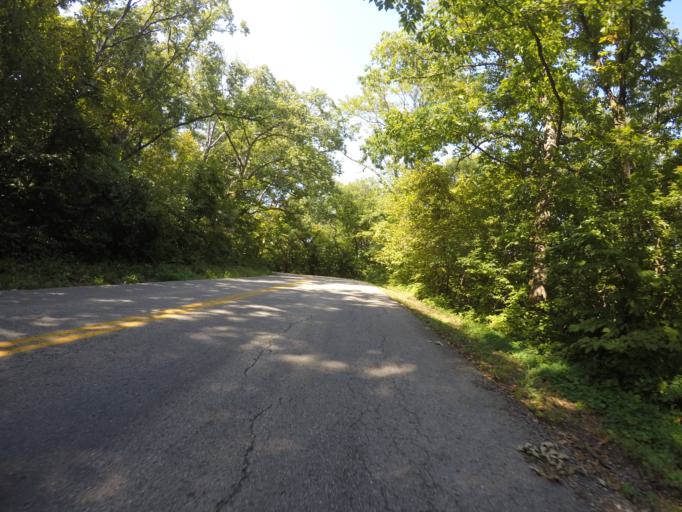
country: US
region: Missouri
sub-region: Platte County
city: Parkville
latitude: 39.1582
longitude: -94.7783
